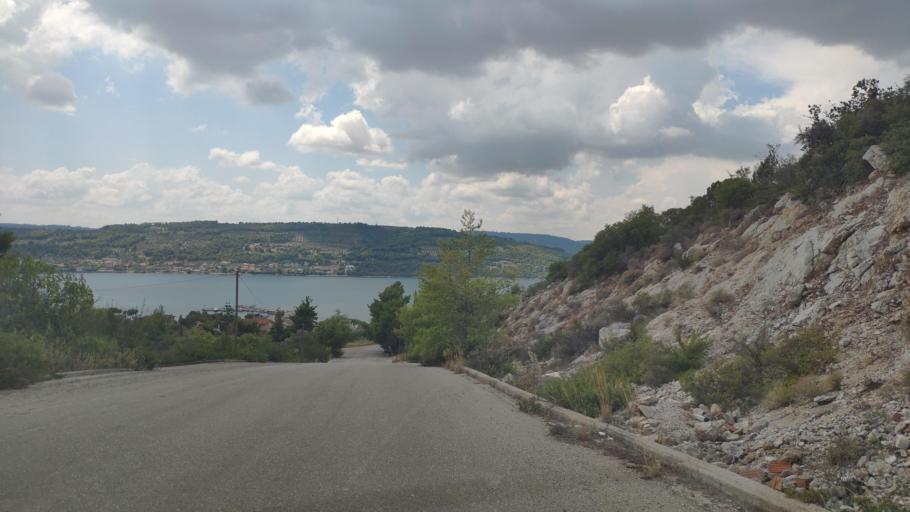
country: GR
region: Central Greece
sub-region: Nomos Fthiotidos
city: Malesina
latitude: 38.6677
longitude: 23.1817
